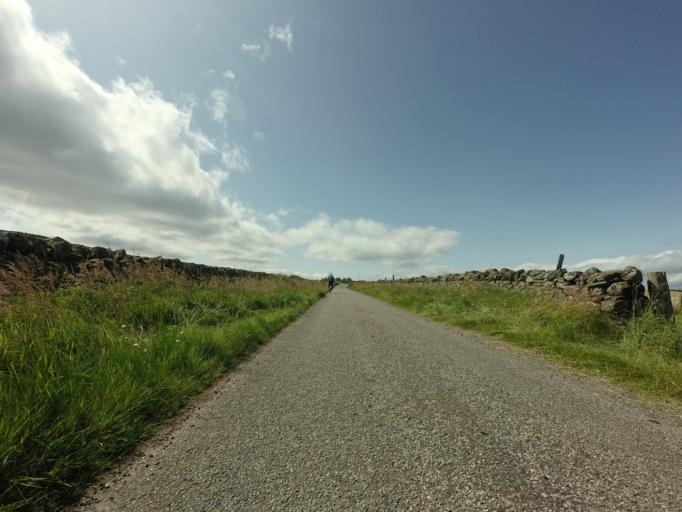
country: GB
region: Scotland
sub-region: Highland
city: Fortrose
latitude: 57.4870
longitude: -4.0243
